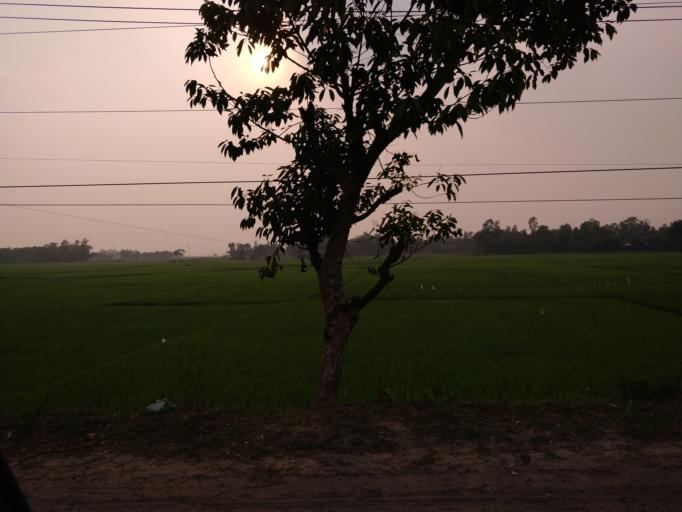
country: BD
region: Sylhet
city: Habiganj
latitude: 24.1672
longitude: 91.3491
